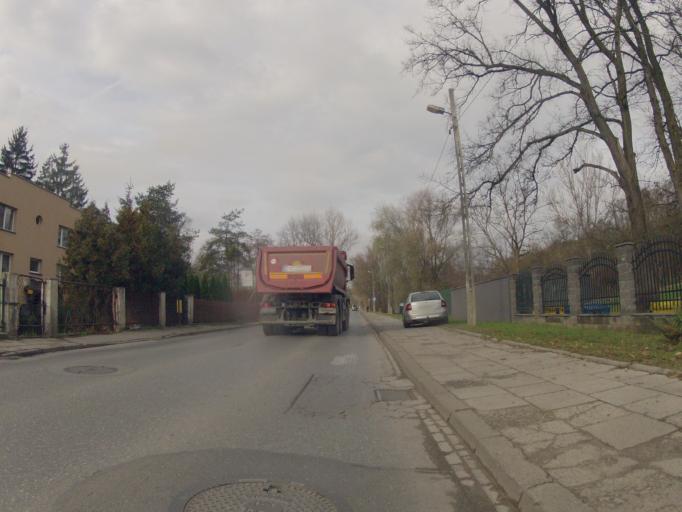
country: PL
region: Lesser Poland Voivodeship
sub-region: Powiat krakowski
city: Rzaska
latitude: 50.0869
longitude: 19.8417
